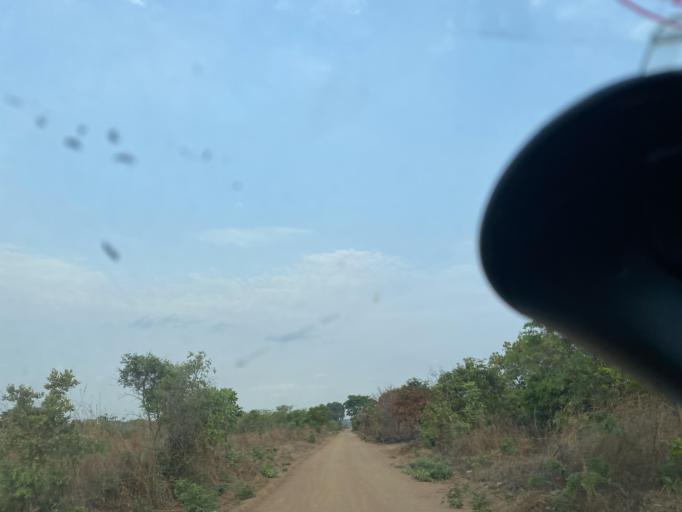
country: ZM
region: Lusaka
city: Chongwe
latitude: -15.2024
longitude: 28.5242
